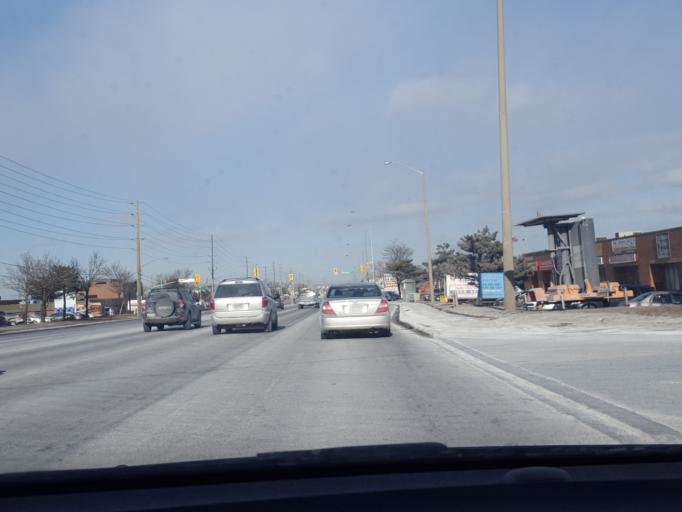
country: CA
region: Ontario
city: Brampton
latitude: 43.7094
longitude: -79.6851
